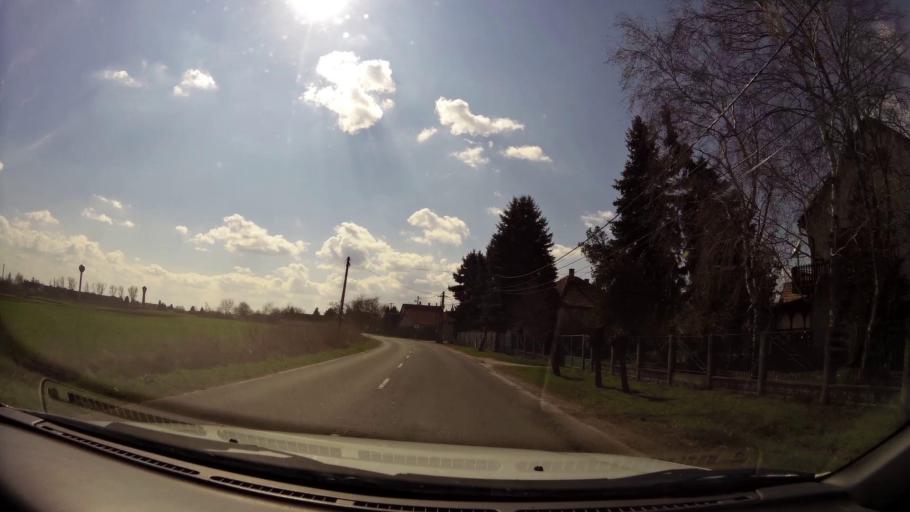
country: HU
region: Pest
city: Tapioszele
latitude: 47.3319
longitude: 19.8847
